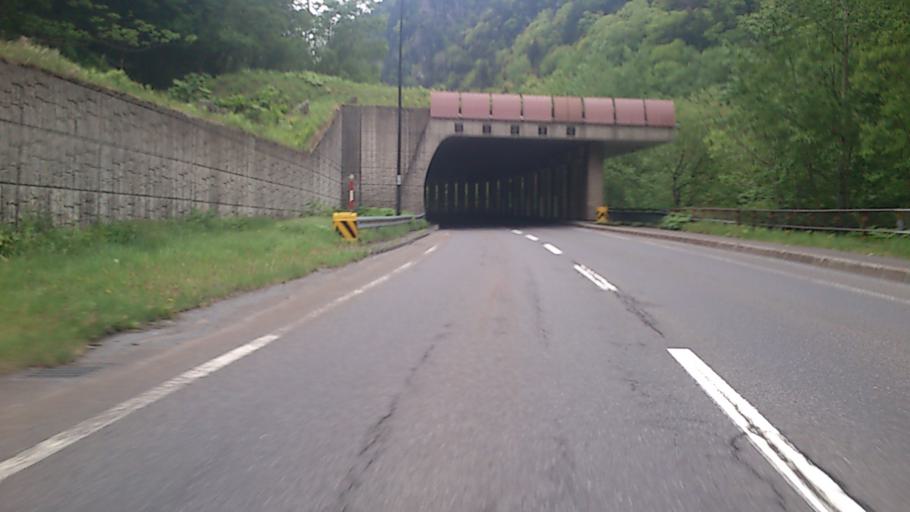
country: JP
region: Hokkaido
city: Kamikawa
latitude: 43.7436
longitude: 142.9358
